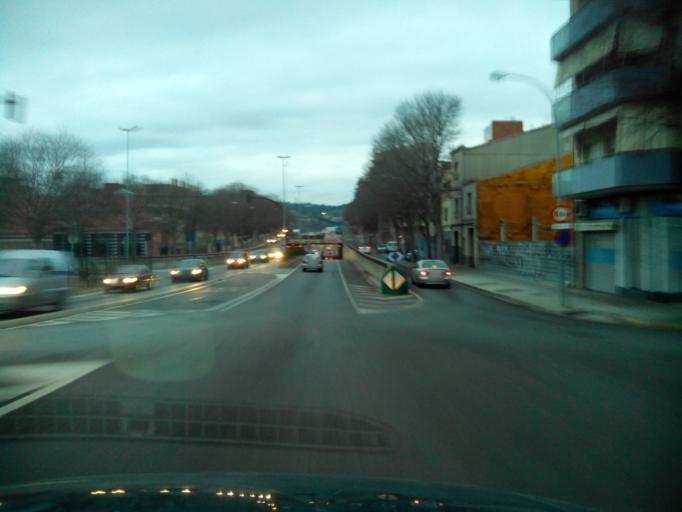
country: ES
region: Catalonia
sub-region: Provincia de Barcelona
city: Terrassa
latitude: 41.5514
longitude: 2.0224
